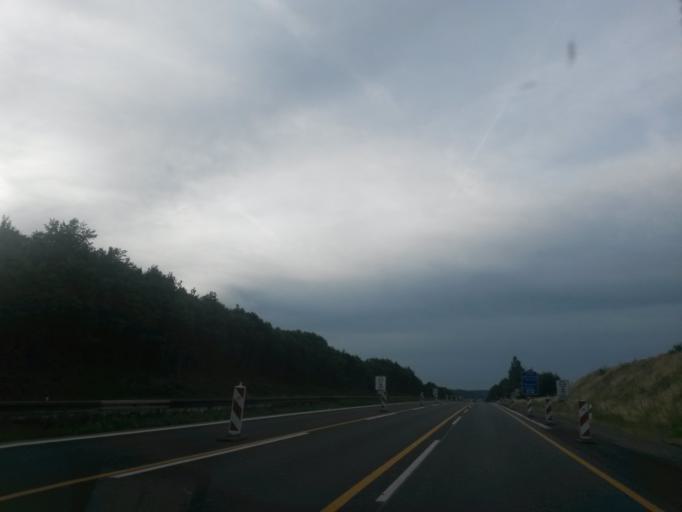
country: DE
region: Bavaria
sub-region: Regierungsbezirk Mittelfranken
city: Greding
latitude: 49.0719
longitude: 11.3019
